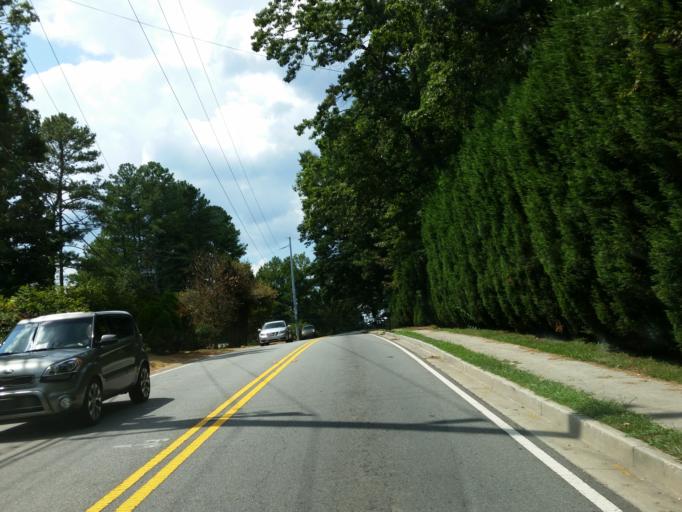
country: US
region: Georgia
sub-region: Fulton County
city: Roswell
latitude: 34.0263
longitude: -84.4129
